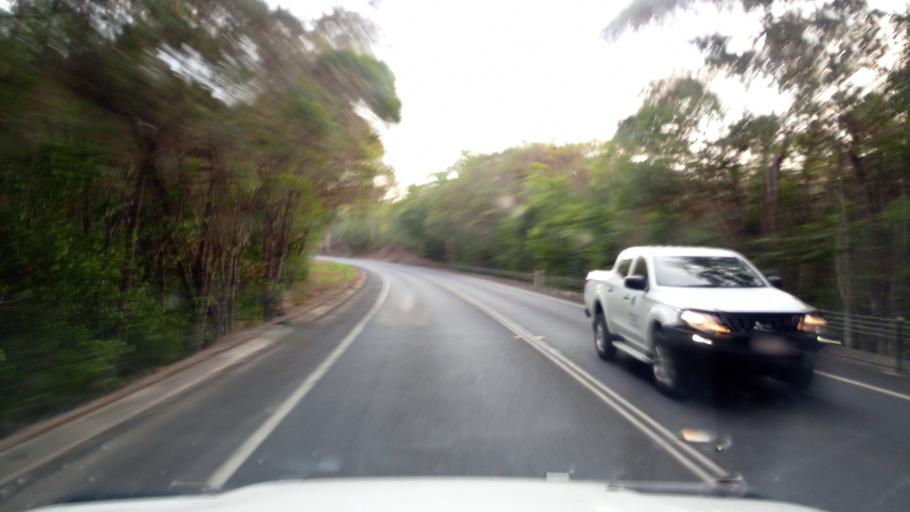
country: AU
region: Queensland
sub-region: Tablelands
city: Kuranda
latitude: -16.8489
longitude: 145.6019
